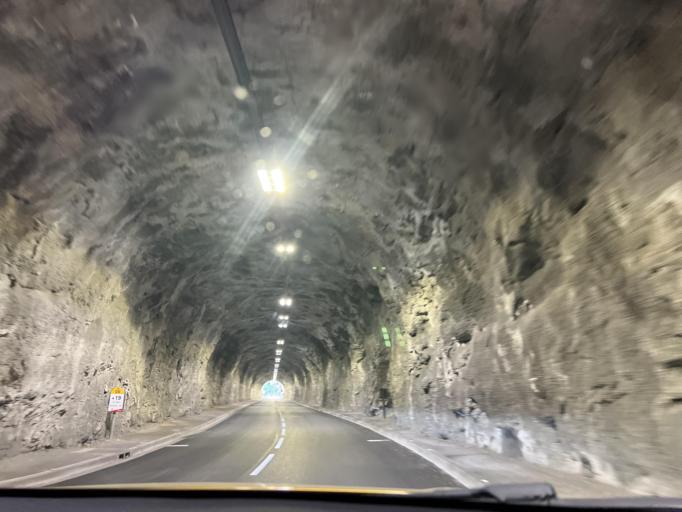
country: FR
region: Provence-Alpes-Cote d'Azur
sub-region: Departement des Alpes-Maritimes
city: Tourrettes-sur-Loup
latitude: 43.7364
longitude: 7.0000
